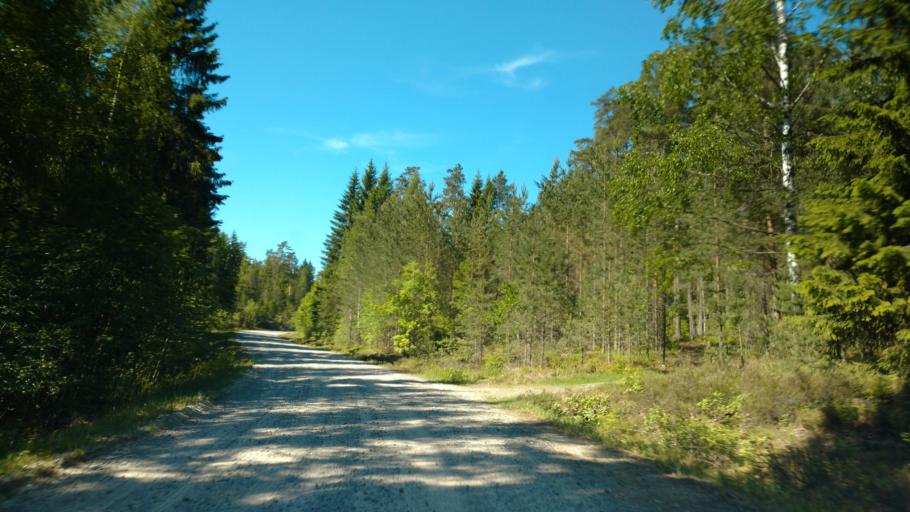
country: FI
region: Varsinais-Suomi
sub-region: Salo
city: Halikko
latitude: 60.4282
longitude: 22.9599
